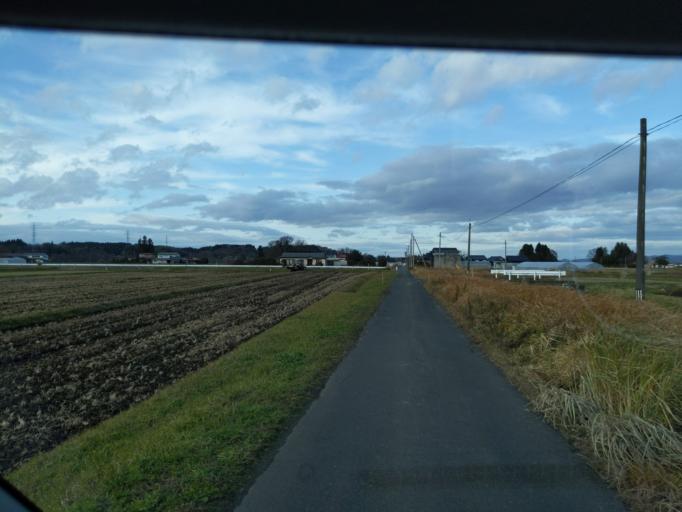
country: JP
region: Iwate
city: Mizusawa
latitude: 39.1559
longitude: 141.0892
